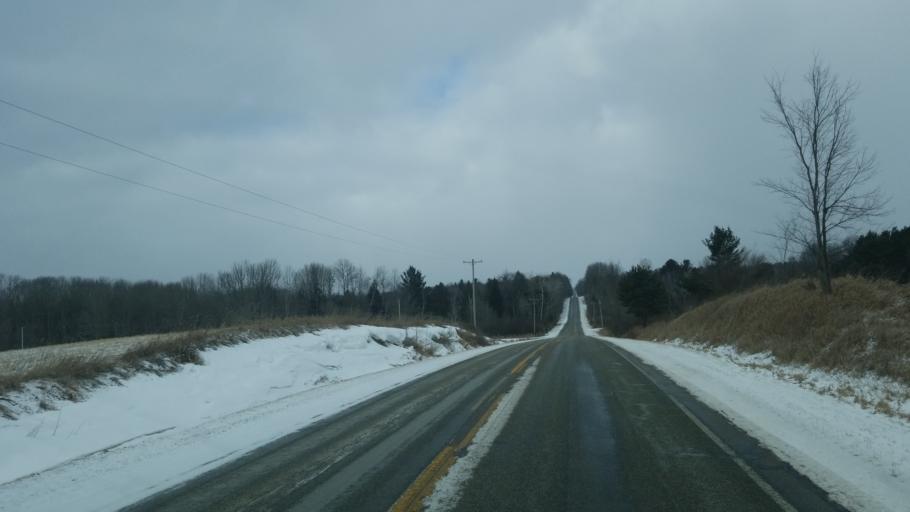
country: US
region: Michigan
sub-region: Osceola County
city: Evart
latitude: 43.9495
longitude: -85.2469
